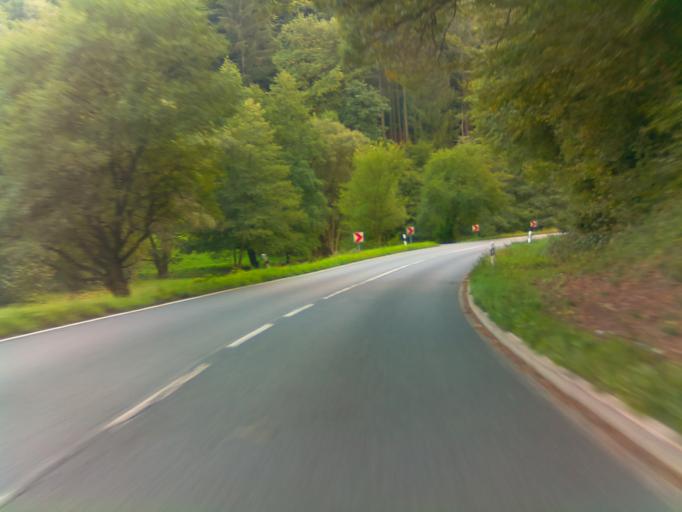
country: DE
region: Baden-Wuerttemberg
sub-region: Karlsruhe Region
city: Wilhelmsfeld
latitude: 49.4836
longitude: 8.7315
